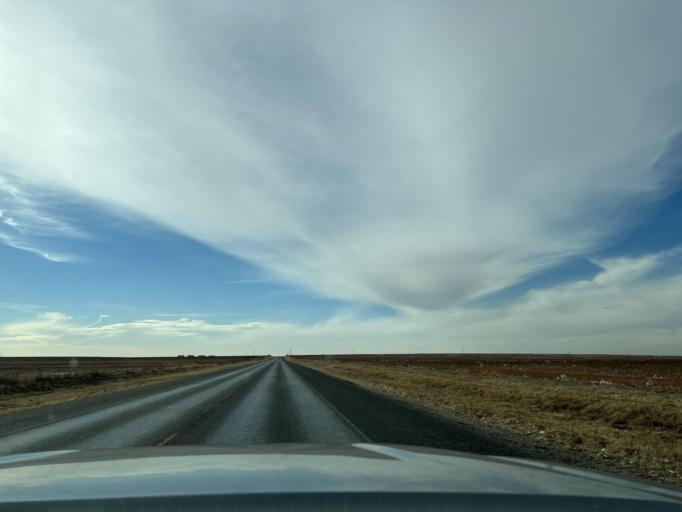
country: US
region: Texas
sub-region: Fisher County
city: Roby
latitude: 32.7417
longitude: -100.4491
